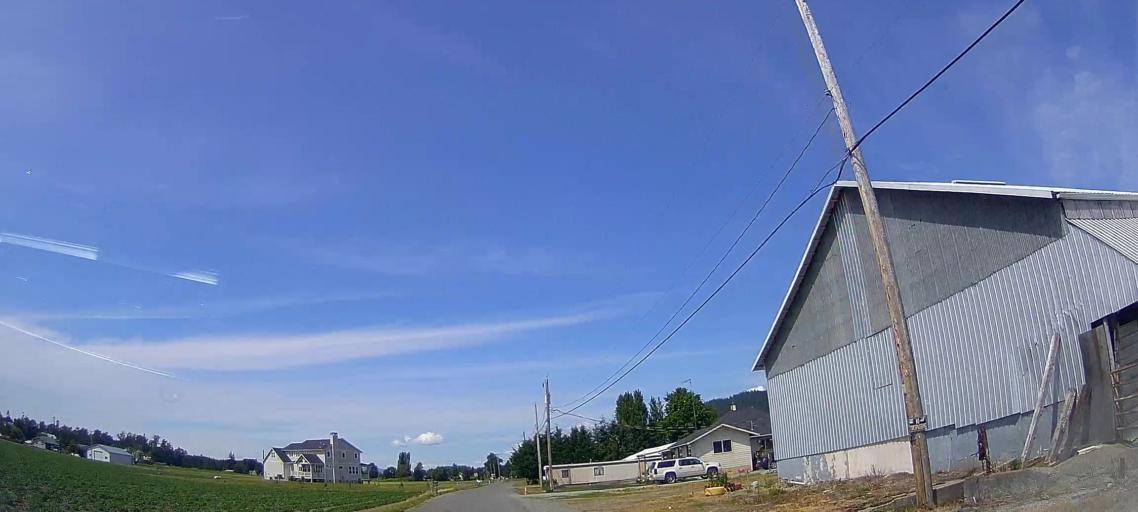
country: US
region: Washington
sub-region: Skagit County
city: Mount Vernon
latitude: 48.3689
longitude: -122.3240
